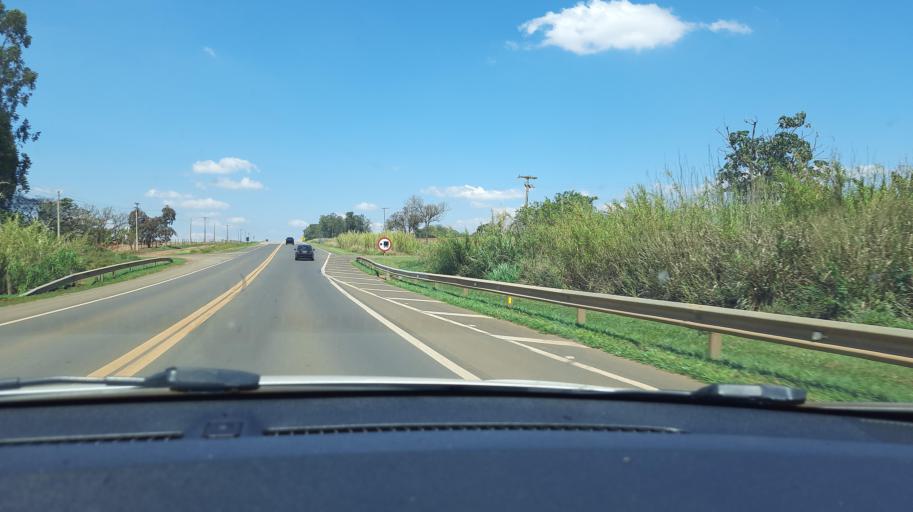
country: BR
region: Sao Paulo
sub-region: Vargem Grande Do Sul
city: Vargem Grande do Sul
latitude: -21.8158
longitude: -46.9777
